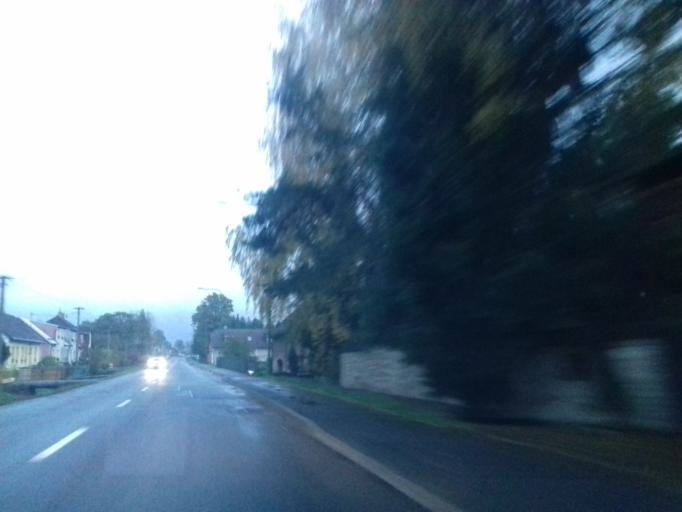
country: CZ
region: Pardubicky
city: Jedlova
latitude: 49.6579
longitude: 16.3155
